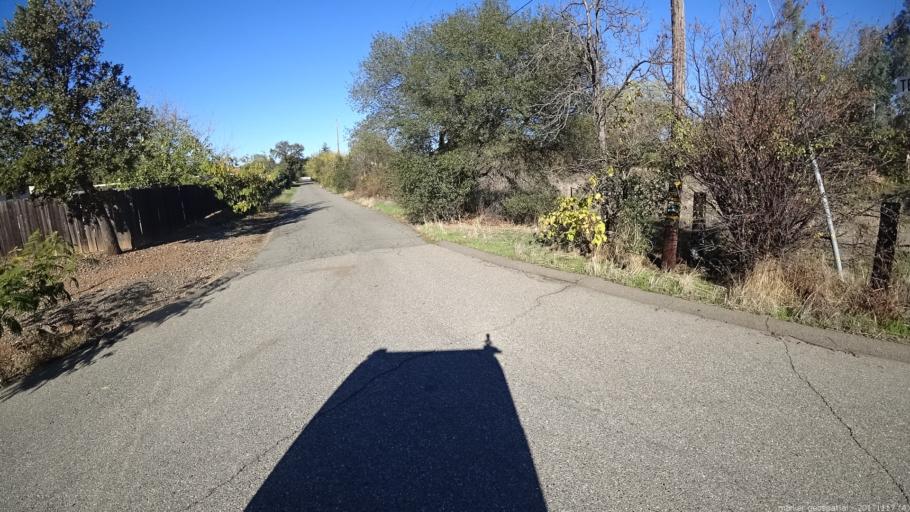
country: US
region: California
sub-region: Shasta County
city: Cottonwood
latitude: 40.3835
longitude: -122.2837
